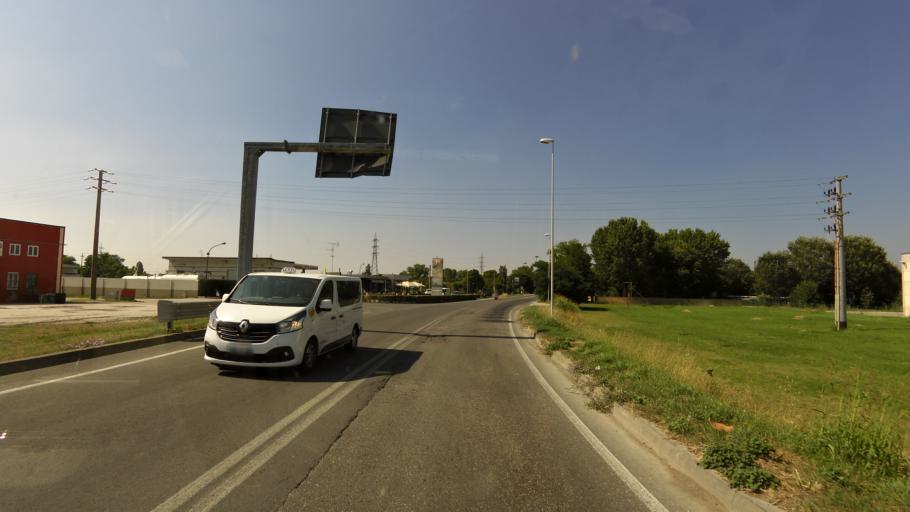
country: IT
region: Emilia-Romagna
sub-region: Provincia di Ravenna
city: Ravenna
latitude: 44.4434
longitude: 12.2108
